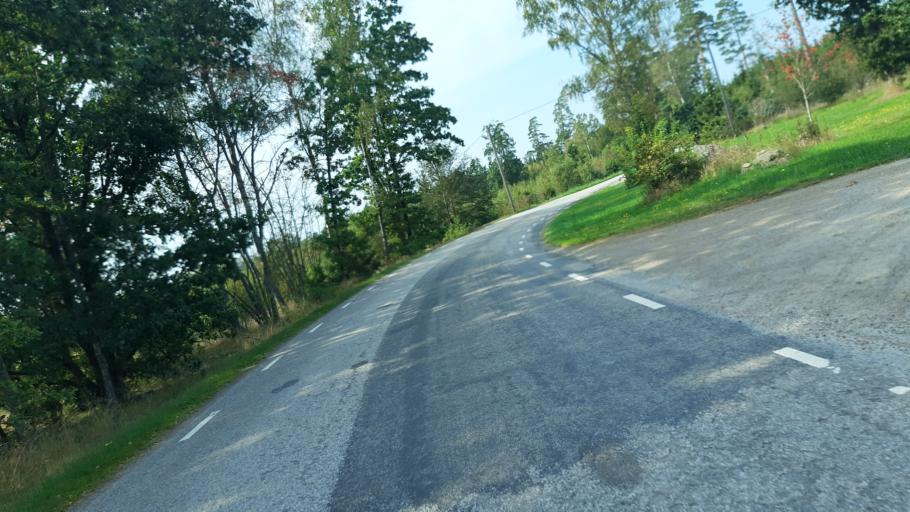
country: SE
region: Blekinge
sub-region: Karlskrona Kommun
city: Nattraby
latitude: 56.2168
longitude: 15.4471
